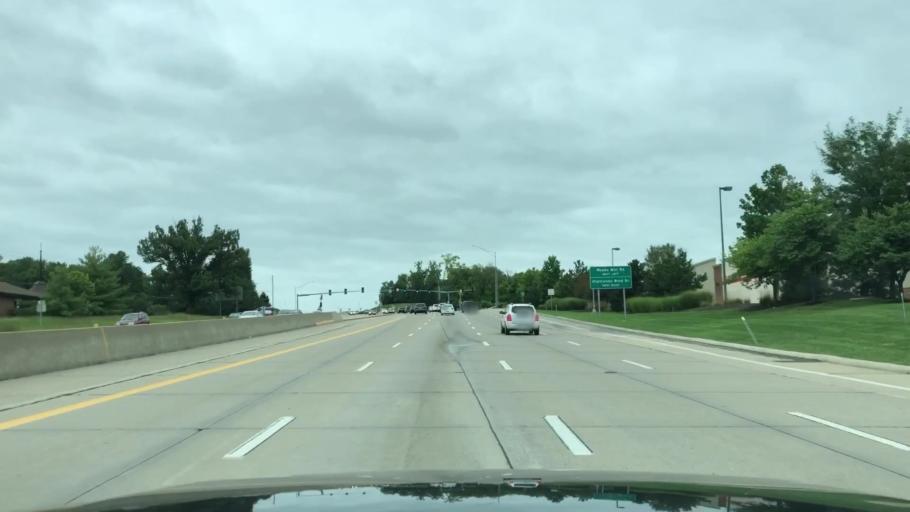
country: US
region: Missouri
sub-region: Saint Louis County
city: Manchester
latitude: 38.5970
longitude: -90.5086
